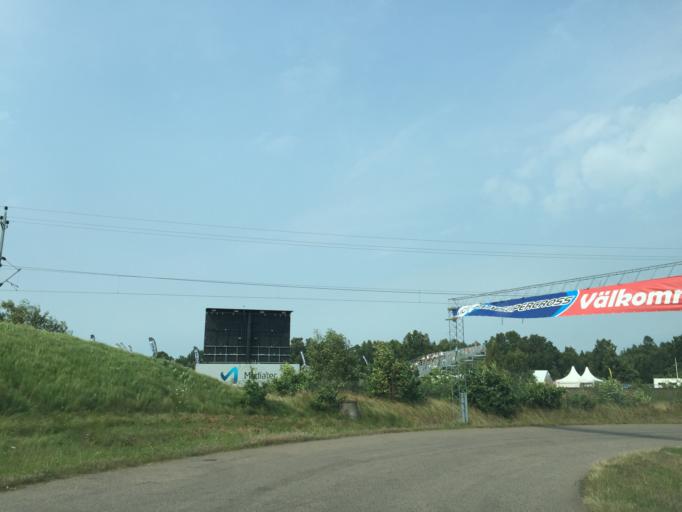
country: SE
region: Skane
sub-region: Angelholms Kommun
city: AEngelholm
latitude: 56.2301
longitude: 12.8322
